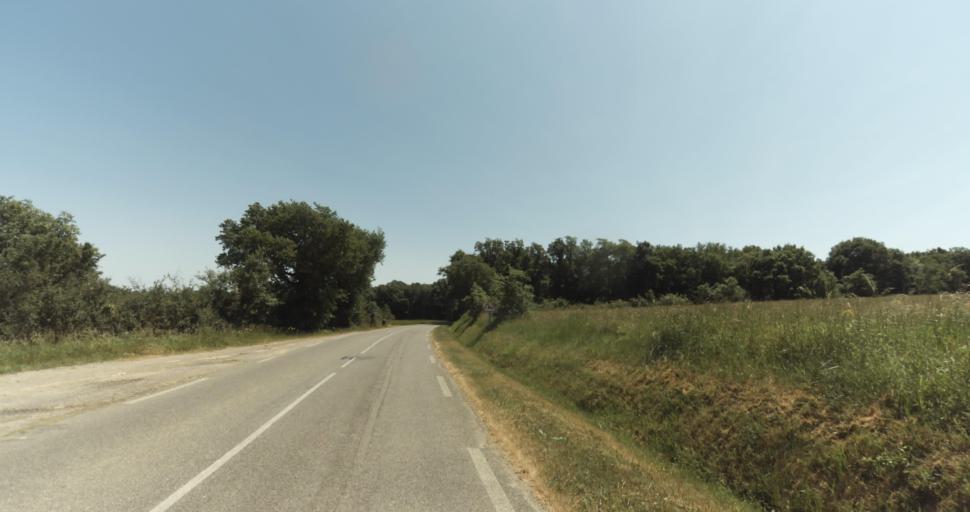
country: FR
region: Midi-Pyrenees
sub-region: Departement de la Haute-Garonne
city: Levignac
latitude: 43.6253
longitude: 1.1857
